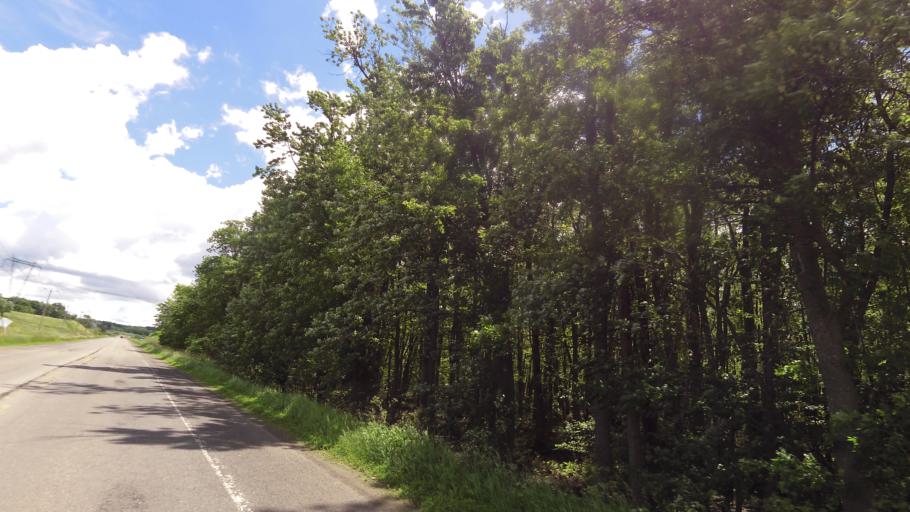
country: CA
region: Quebec
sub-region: Monteregie
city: Rigaud
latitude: 45.5370
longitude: -74.3251
